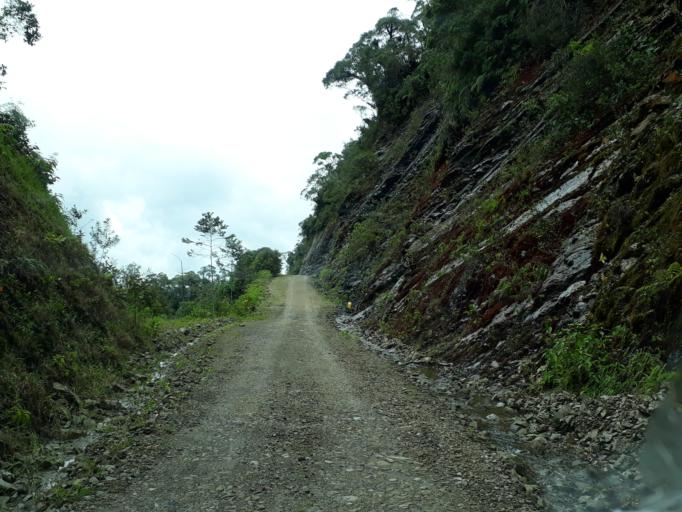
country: CO
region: Cundinamarca
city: Gachala
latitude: 4.7082
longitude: -73.3978
